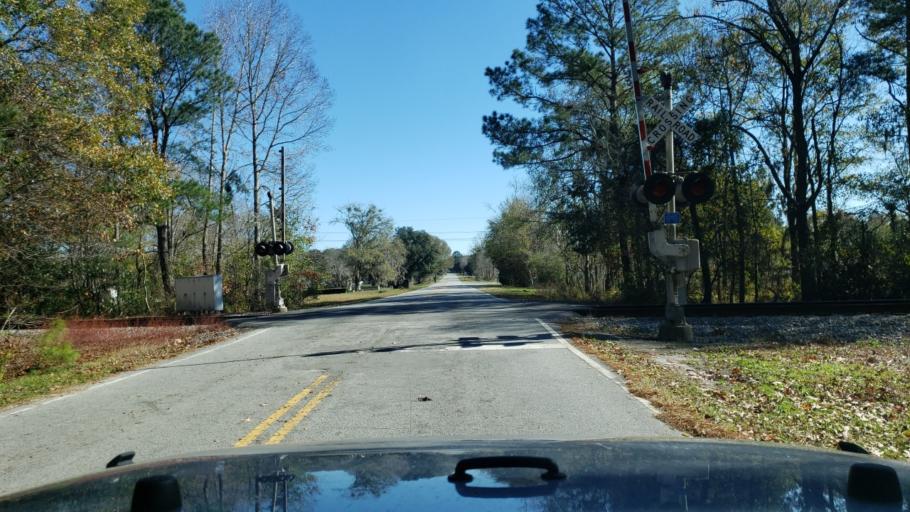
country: US
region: Georgia
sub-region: Chatham County
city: Georgetown
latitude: 32.0315
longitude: -81.1822
